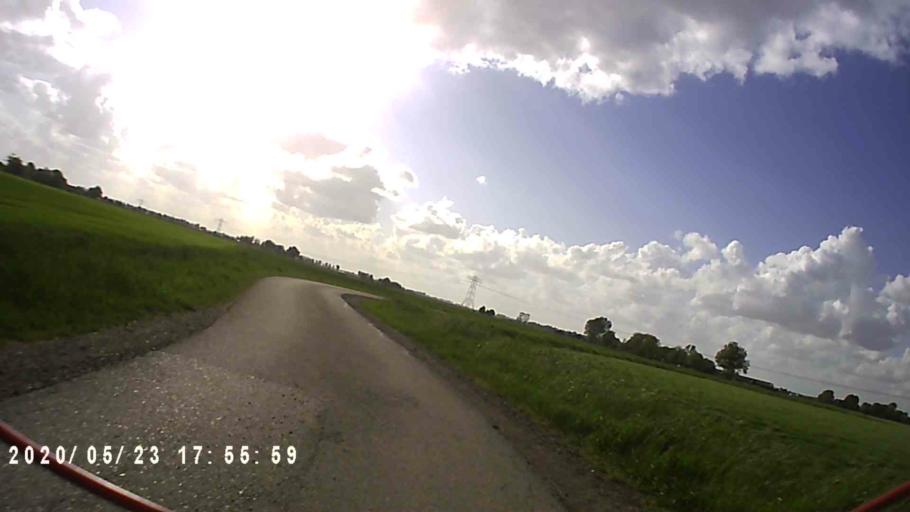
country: NL
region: Groningen
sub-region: Gemeente Slochteren
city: Slochteren
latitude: 53.2495
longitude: 6.7456
